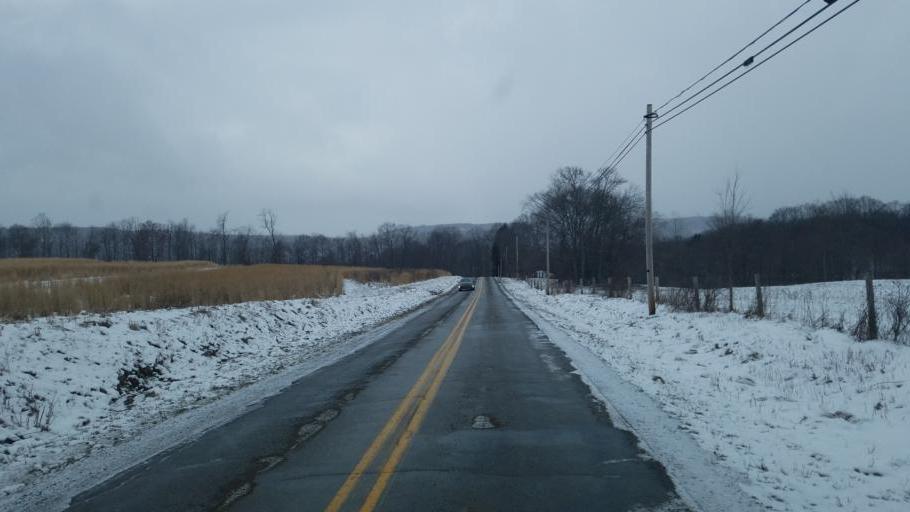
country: US
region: Pennsylvania
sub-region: Crawford County
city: Cochranton
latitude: 41.4768
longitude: -80.0021
